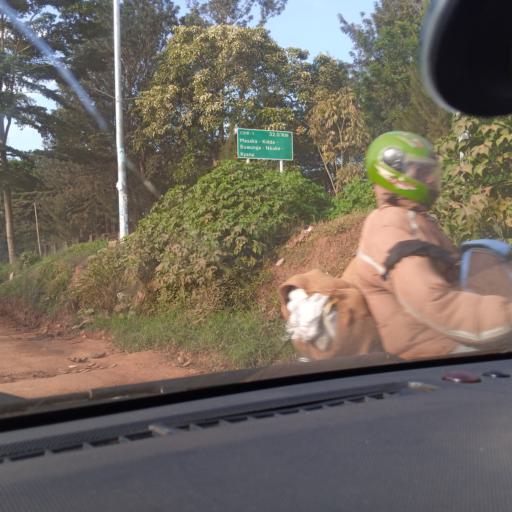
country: UG
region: Central Region
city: Masaka
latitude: -0.3484
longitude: 31.7391
